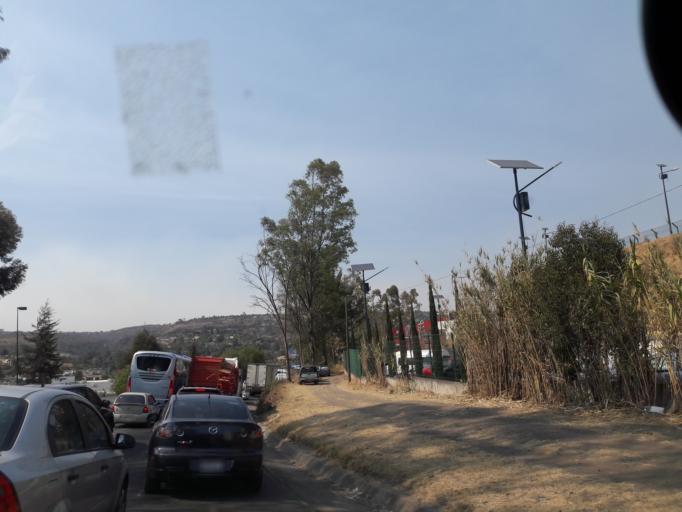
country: MX
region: Tlaxcala
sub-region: Apetatitlan de Antonio Carvajal
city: Tlatempan
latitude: 19.3373
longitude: -98.1993
